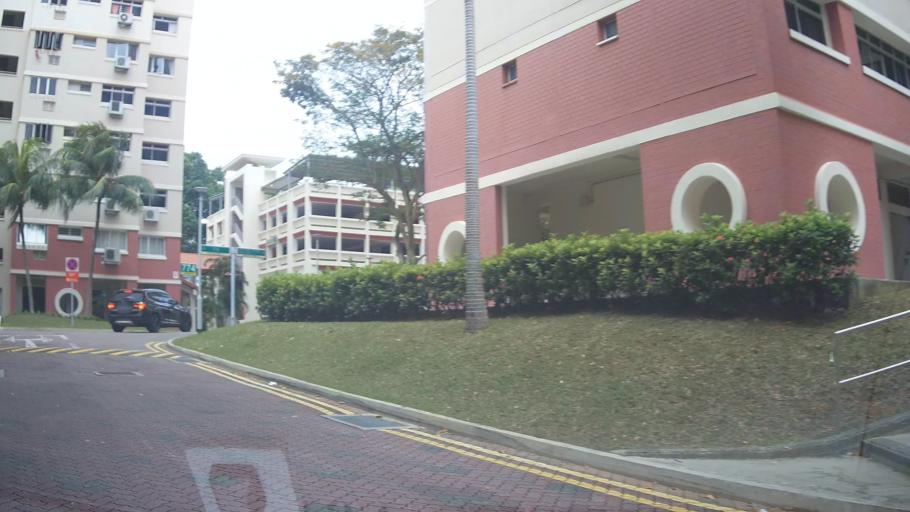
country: MY
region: Johor
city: Kampung Pasir Gudang Baru
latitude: 1.3741
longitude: 103.9373
